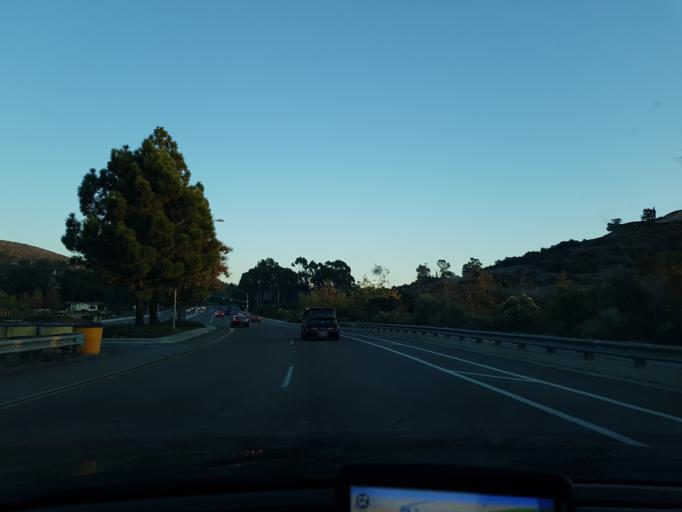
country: US
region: California
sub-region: San Diego County
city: Fairbanks Ranch
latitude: 32.9394
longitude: -117.1289
